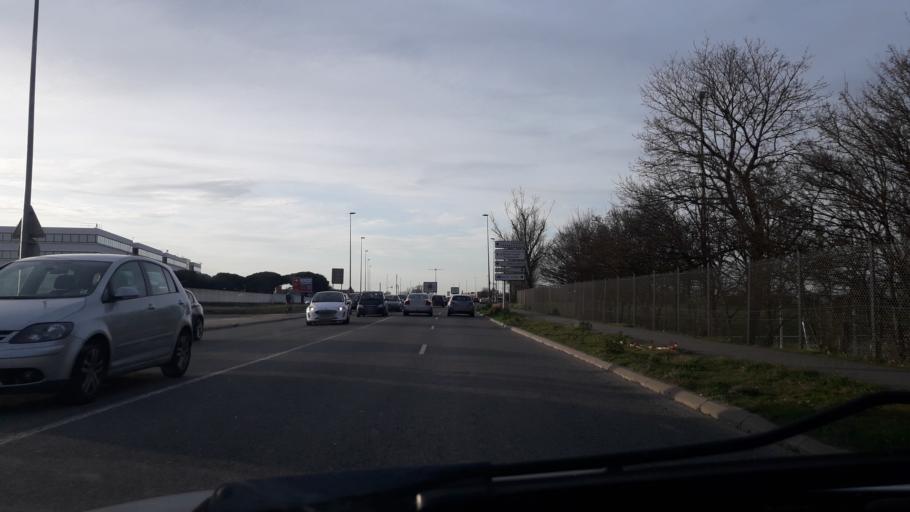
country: FR
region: Midi-Pyrenees
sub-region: Departement de la Haute-Garonne
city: Portet-sur-Garonne
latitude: 43.5605
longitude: 1.3937
